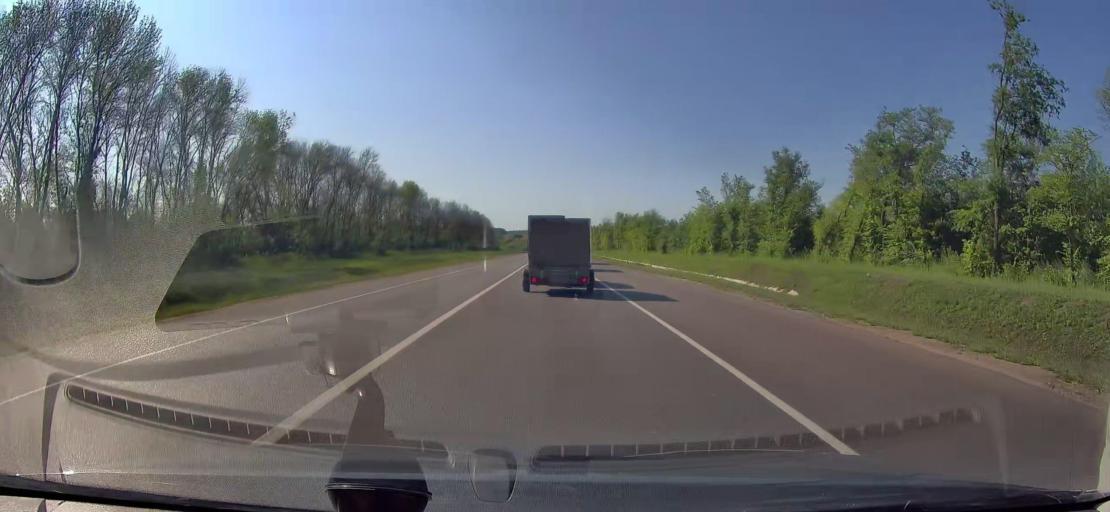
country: RU
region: Orjol
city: Kromy
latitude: 52.6278
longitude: 35.7553
